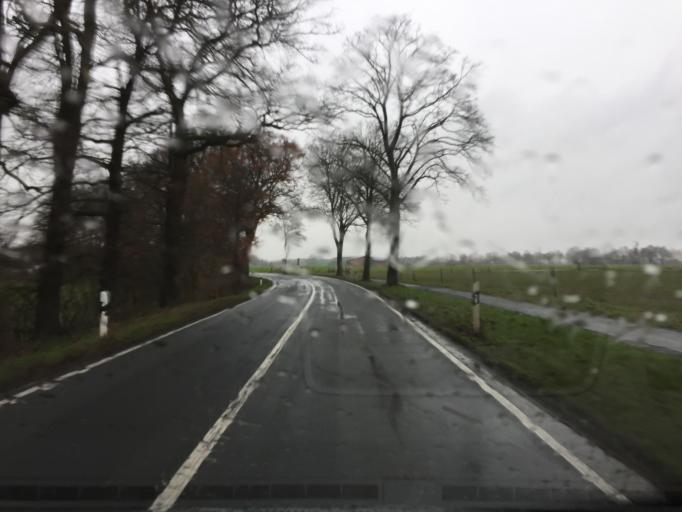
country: DE
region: Lower Saxony
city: Borstel
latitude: 52.6050
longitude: 8.9388
